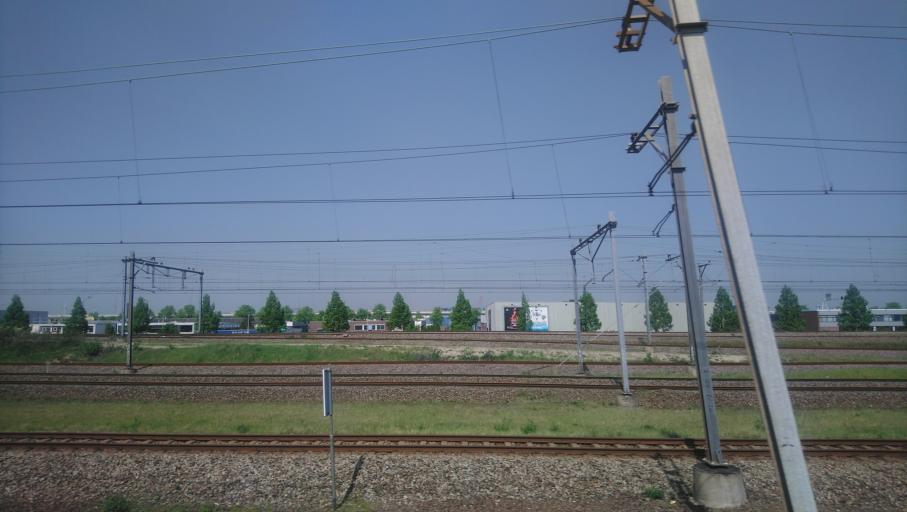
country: NL
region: North Holland
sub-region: Gemeente Zaanstad
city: Zaandam
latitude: 52.3890
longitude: 4.8248
